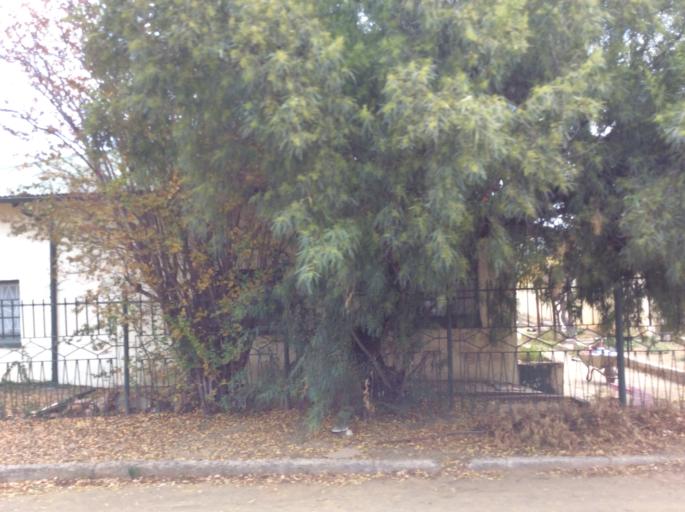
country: LS
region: Mafeteng
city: Mafeteng
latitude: -29.7303
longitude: 27.0430
